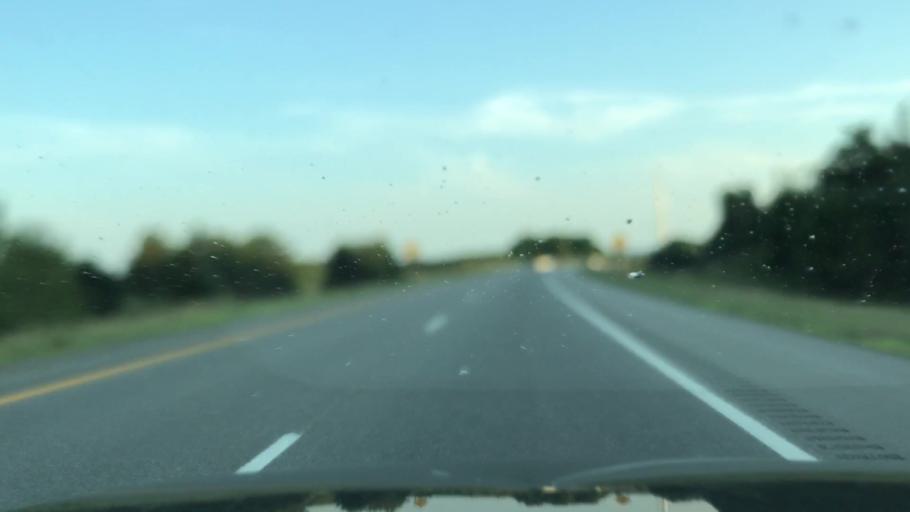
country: US
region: Michigan
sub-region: Osceola County
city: Reed City
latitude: 43.8470
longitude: -85.5322
